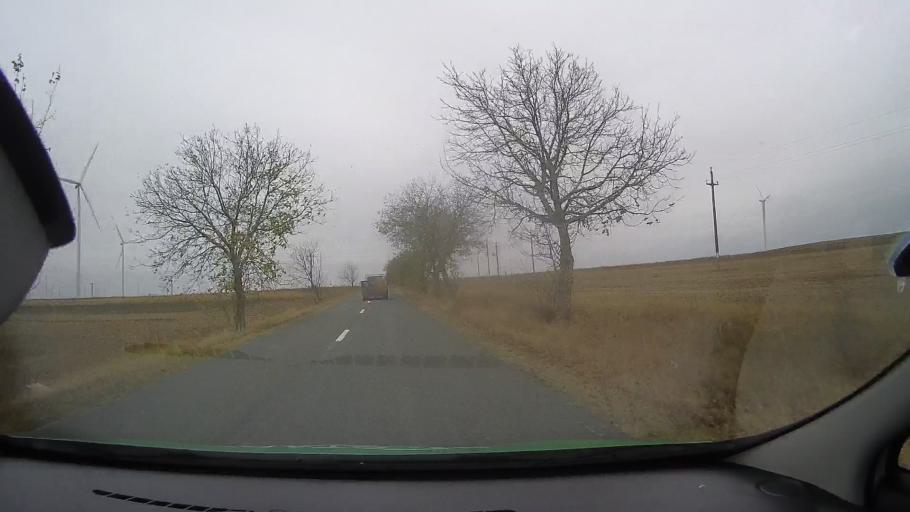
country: RO
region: Constanta
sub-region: Comuna Targusor
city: Targusor
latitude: 44.4786
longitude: 28.3762
